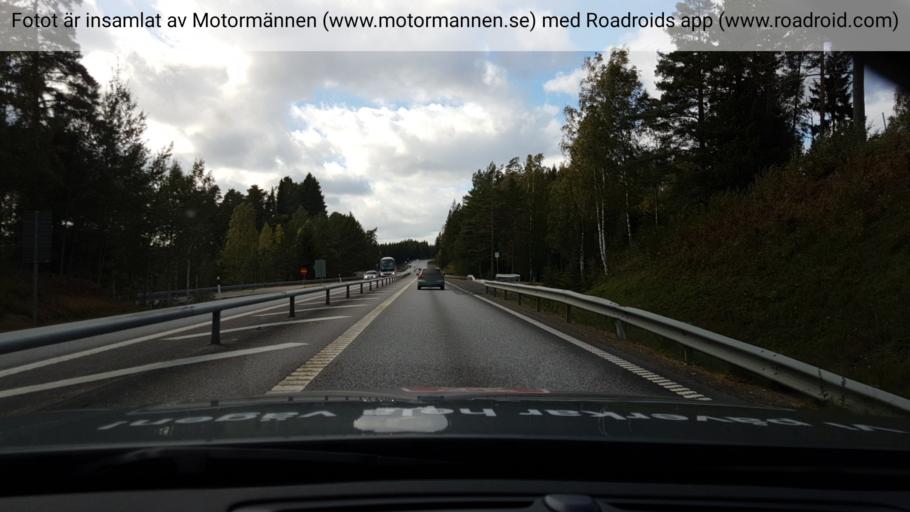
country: SE
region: OErebro
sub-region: Karlskoga Kommun
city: Karlskoga
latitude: 59.2954
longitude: 14.6604
